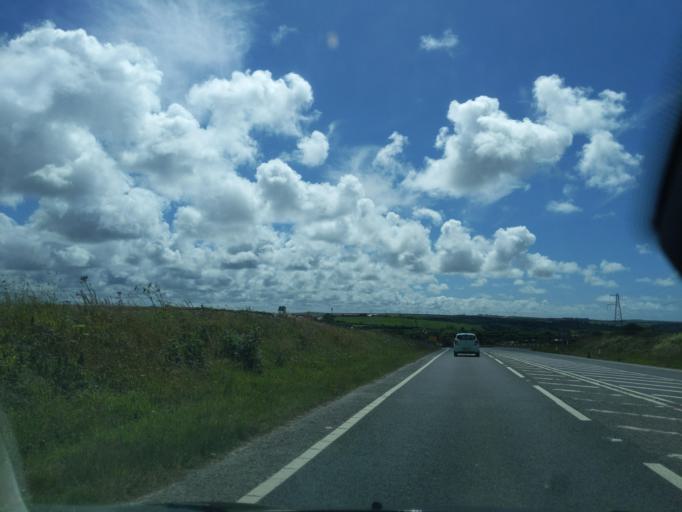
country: GB
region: England
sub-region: Cornwall
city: Truro
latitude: 50.3145
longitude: -5.0894
